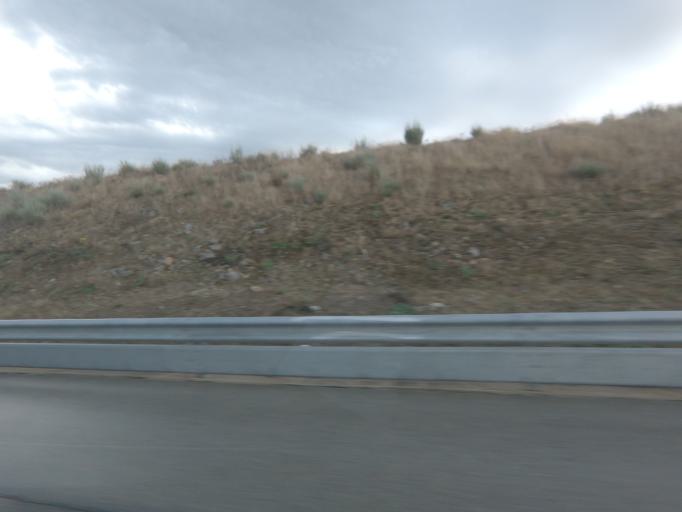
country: PT
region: Viseu
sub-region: Tarouca
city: Tarouca
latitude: 41.0292
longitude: -7.8685
